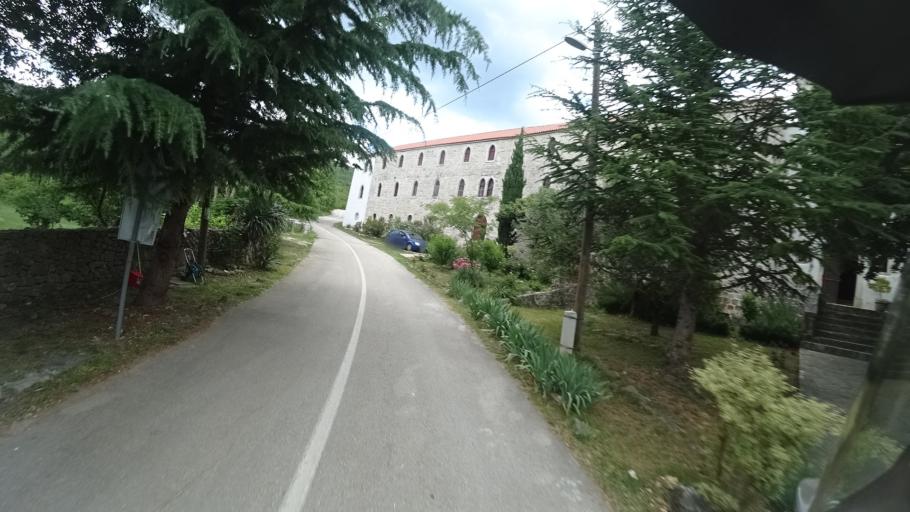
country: HR
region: Zadarska
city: Gracac
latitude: 44.1917
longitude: 15.8871
